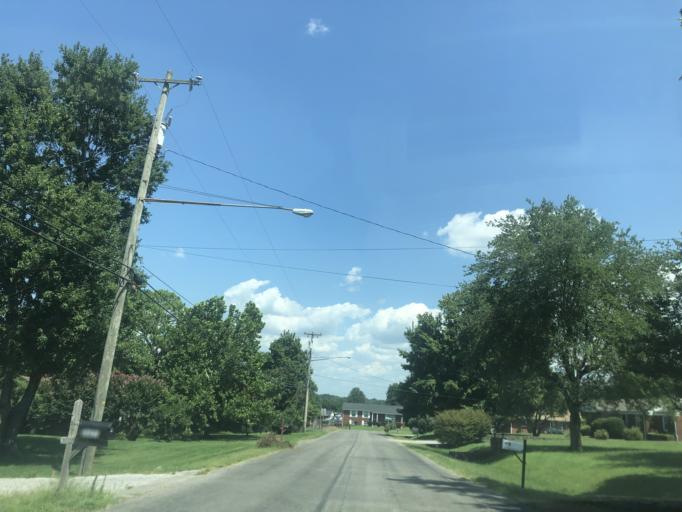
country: US
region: Tennessee
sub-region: Davidson County
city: Nashville
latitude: 36.1877
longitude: -86.7113
